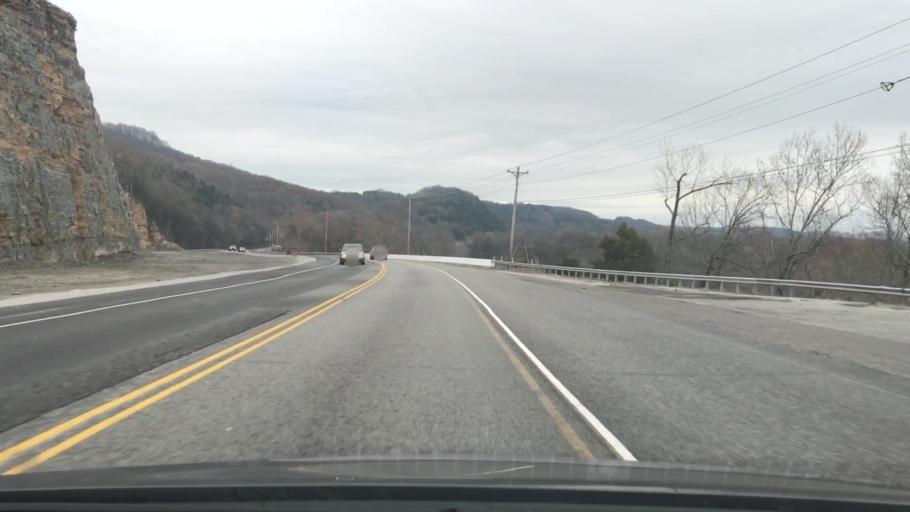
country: US
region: Tennessee
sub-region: Smith County
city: Carthage
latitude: 36.2699
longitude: -85.9810
